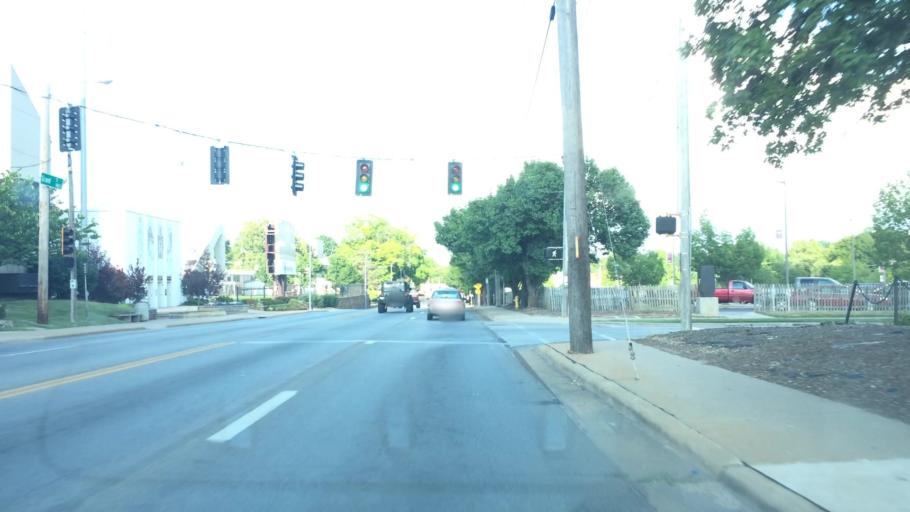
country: US
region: Missouri
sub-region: Greene County
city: Springfield
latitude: 37.1967
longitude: -93.2813
